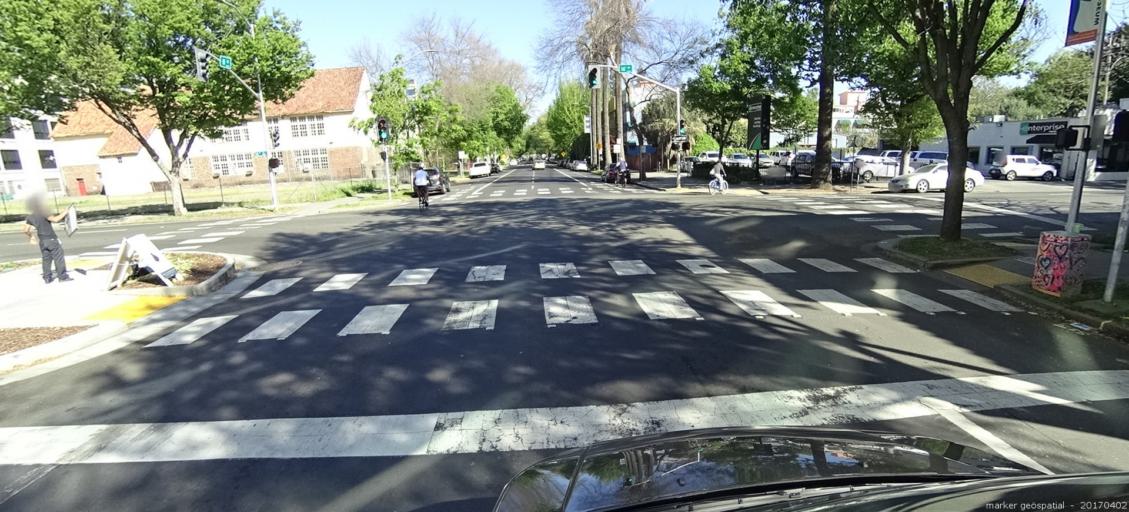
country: US
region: California
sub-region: Sacramento County
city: Sacramento
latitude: 38.5737
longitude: -121.4875
